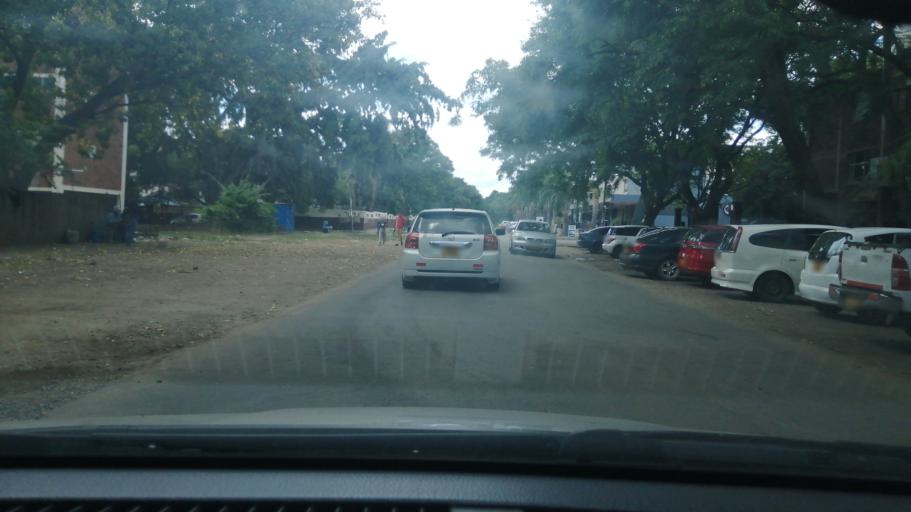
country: ZW
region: Harare
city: Harare
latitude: -17.8199
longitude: 31.0539
